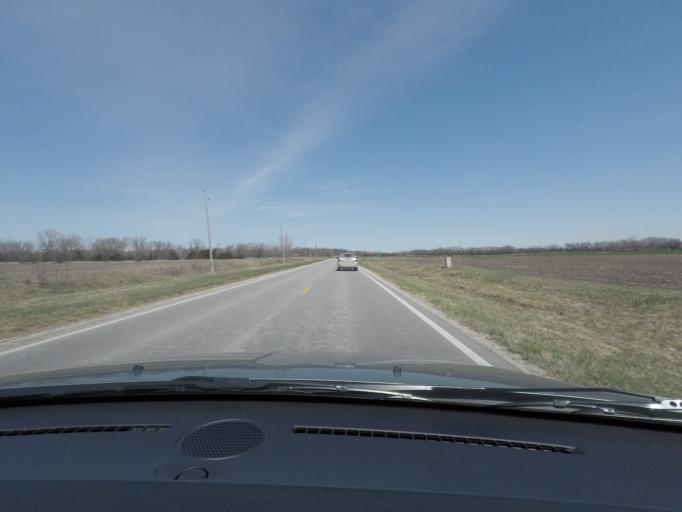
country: US
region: Kansas
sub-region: Lyon County
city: Emporia
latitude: 38.4468
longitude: -96.1706
